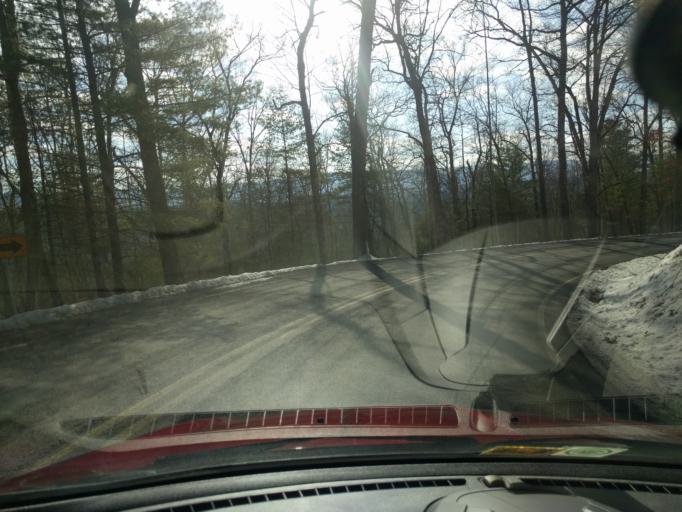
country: US
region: Virginia
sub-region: Bath County
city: Warm Springs
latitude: 38.0880
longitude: -79.8405
